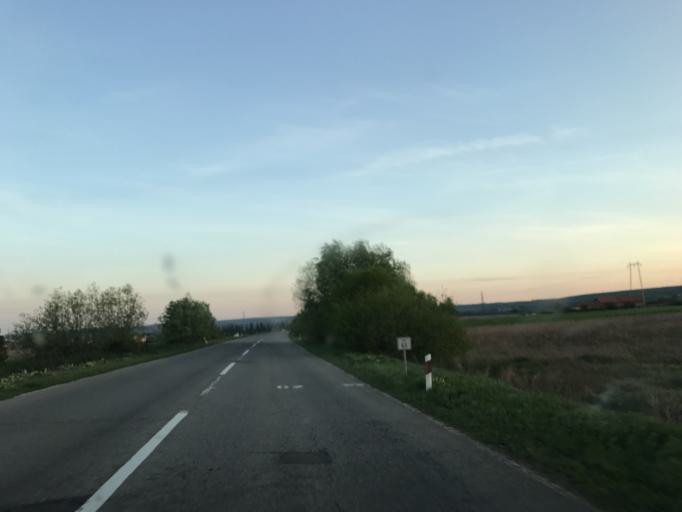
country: RS
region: Central Serbia
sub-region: Borski Okrug
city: Negotin
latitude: 44.2548
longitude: 22.5194
